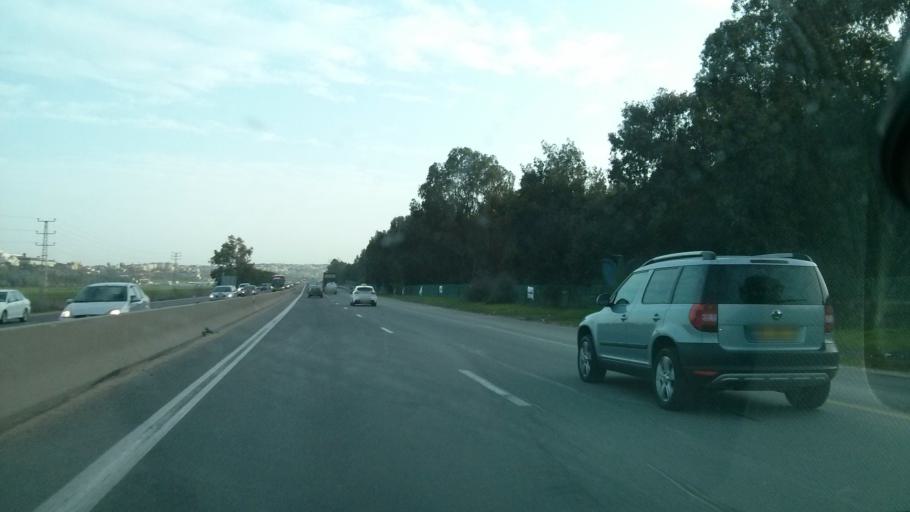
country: PS
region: West Bank
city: Barta`ah ash Sharqiyah
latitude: 32.4890
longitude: 35.0505
